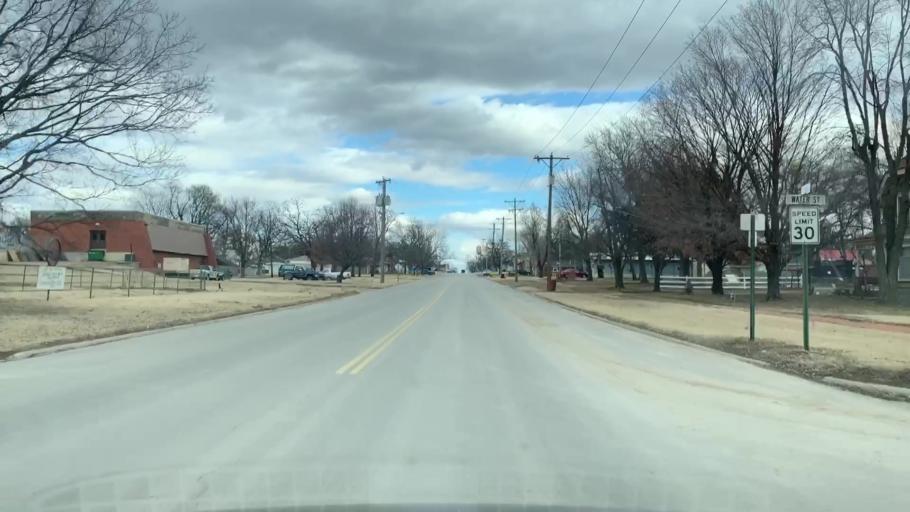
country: US
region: Kansas
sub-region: Allen County
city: Humboldt
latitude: 37.8111
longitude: -95.4468
